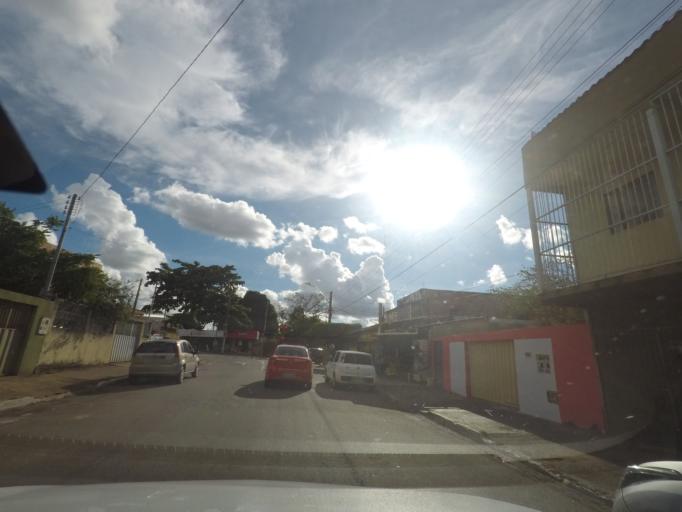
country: BR
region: Goias
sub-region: Goiania
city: Goiania
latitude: -16.7216
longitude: -49.3049
